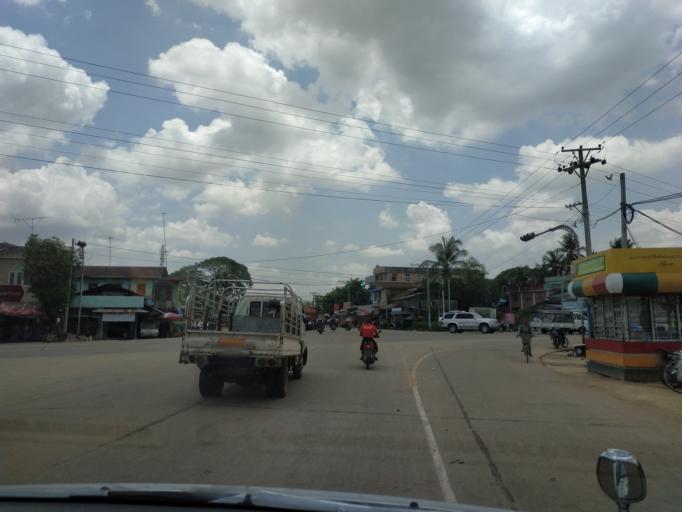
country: MM
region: Bago
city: Bago
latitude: 17.4743
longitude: 96.5271
